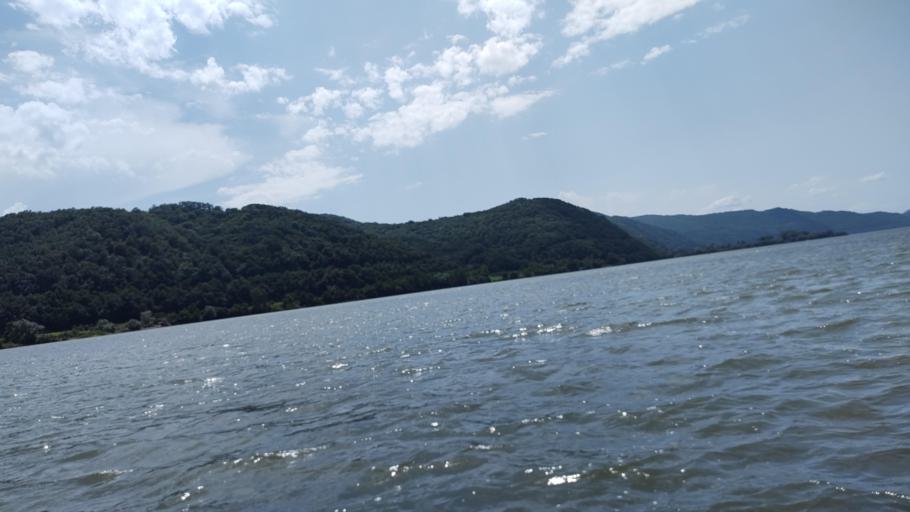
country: RO
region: Caras-Severin
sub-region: Comuna Berzasca
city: Liubcova
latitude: 44.6509
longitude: 21.8687
